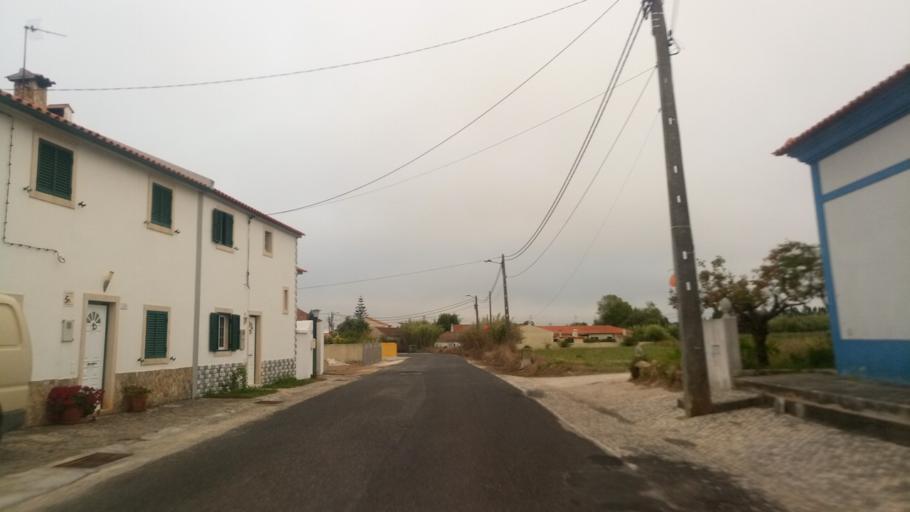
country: PT
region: Leiria
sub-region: Caldas da Rainha
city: Caldas da Rainha
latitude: 39.4528
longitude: -9.1791
